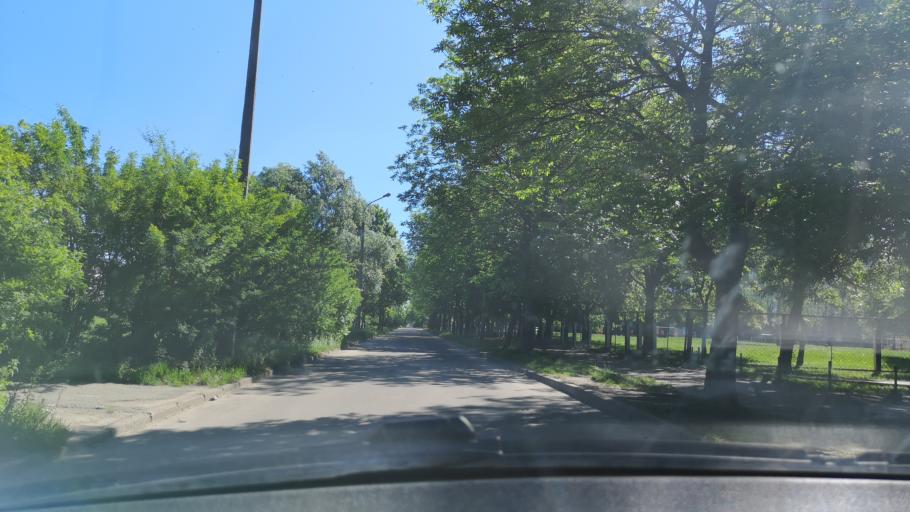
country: BY
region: Brest
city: Brest
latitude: 52.1027
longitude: 23.7532
